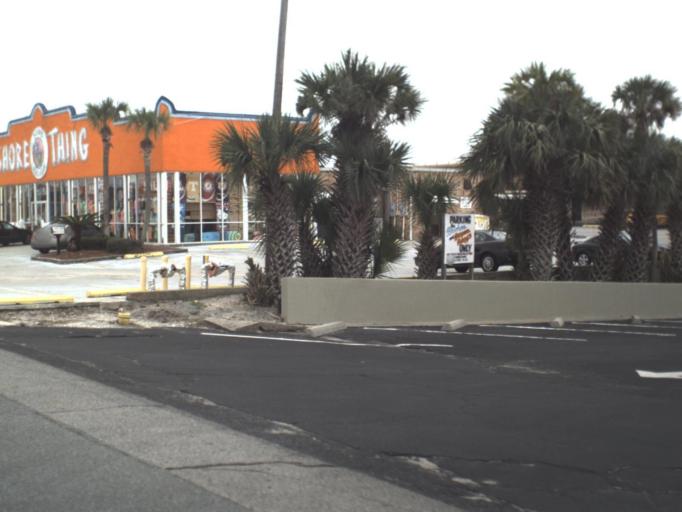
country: US
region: Florida
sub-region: Bay County
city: Panama City Beach
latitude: 30.1933
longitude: -85.8354
